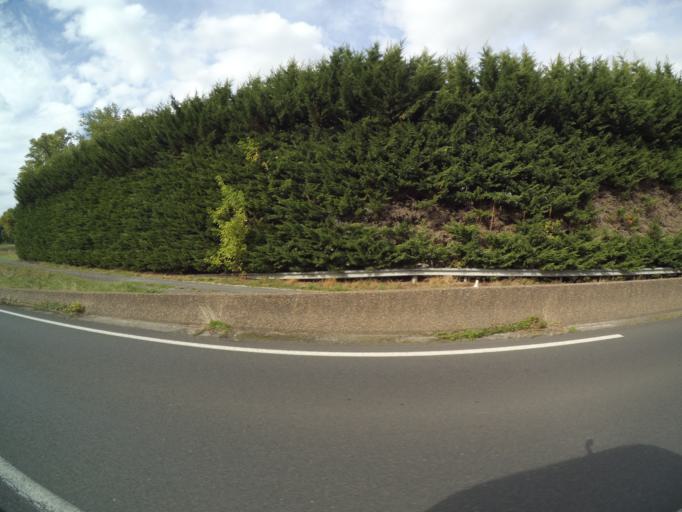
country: FR
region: Centre
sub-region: Departement d'Indre-et-Loire
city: Cinq-Mars-la-Pile
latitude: 47.3297
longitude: 0.4519
